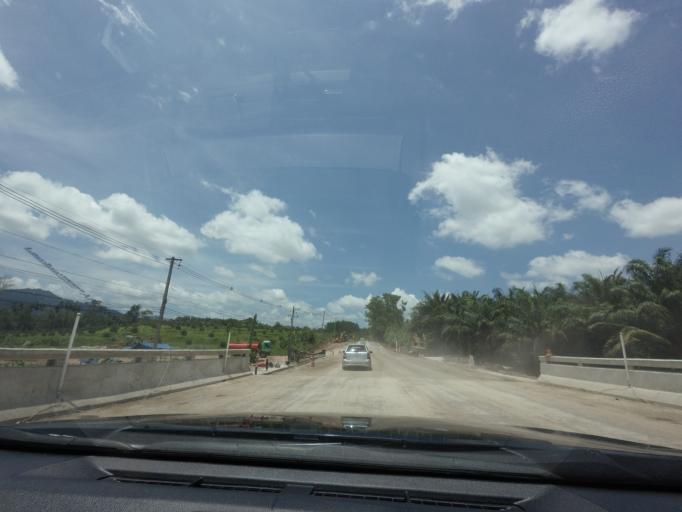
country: TH
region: Chumphon
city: Ban Nam Yuen
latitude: 9.9005
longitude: 98.8936
